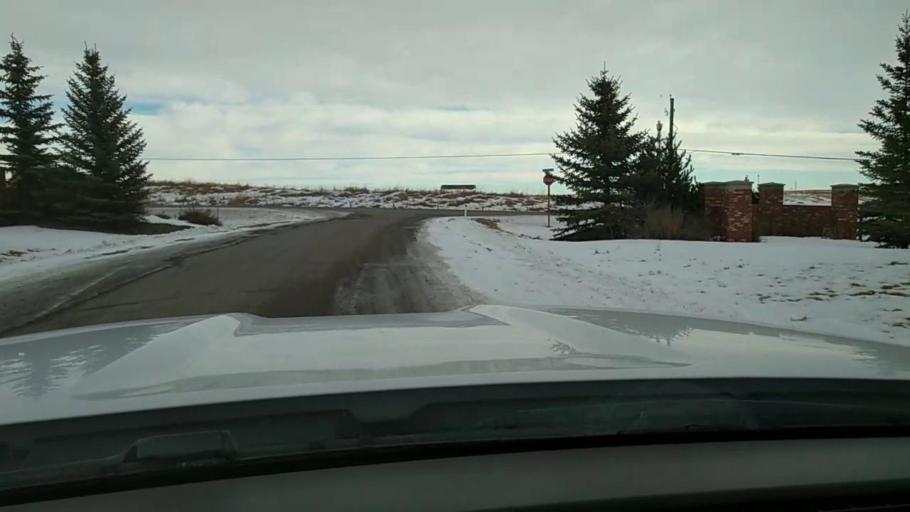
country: CA
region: Alberta
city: Cochrane
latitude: 51.2095
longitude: -114.2815
